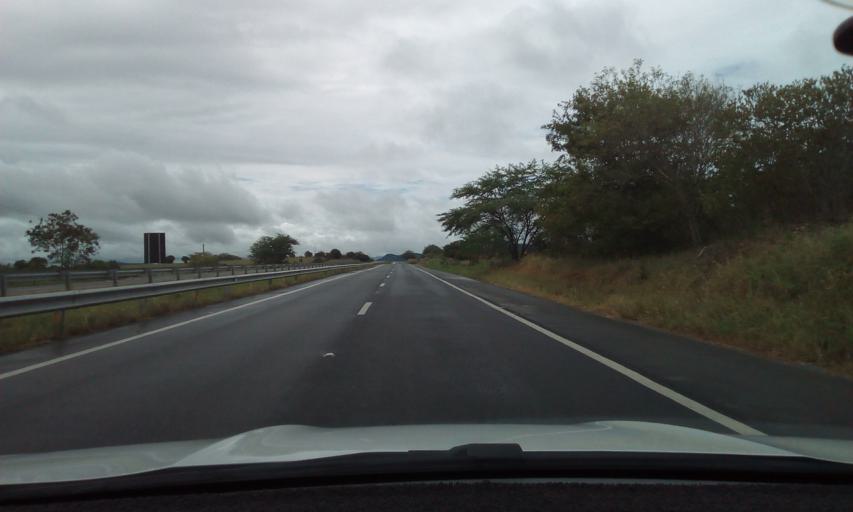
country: BR
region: Paraiba
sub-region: Mogeiro
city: Mogeiro
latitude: -7.2048
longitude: -35.5081
